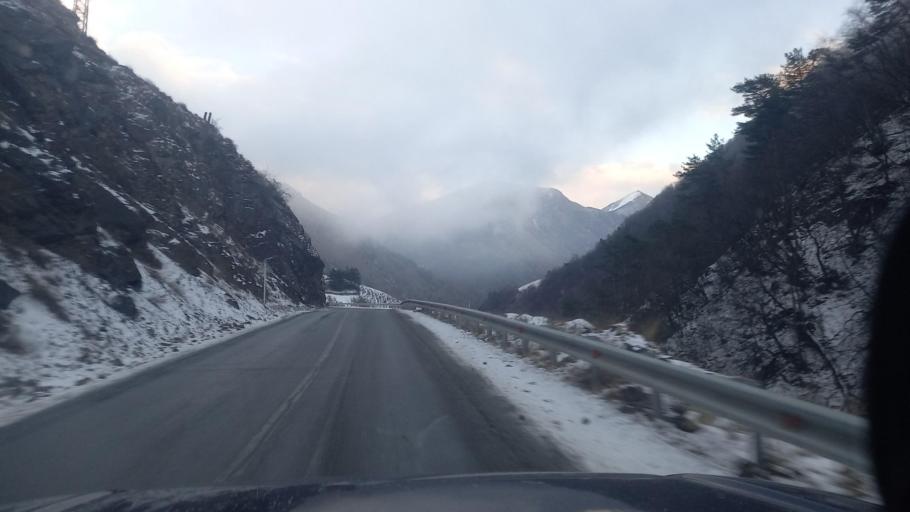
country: RU
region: Ingushetiya
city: Dzhayrakh
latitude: 42.7903
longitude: 44.7759
